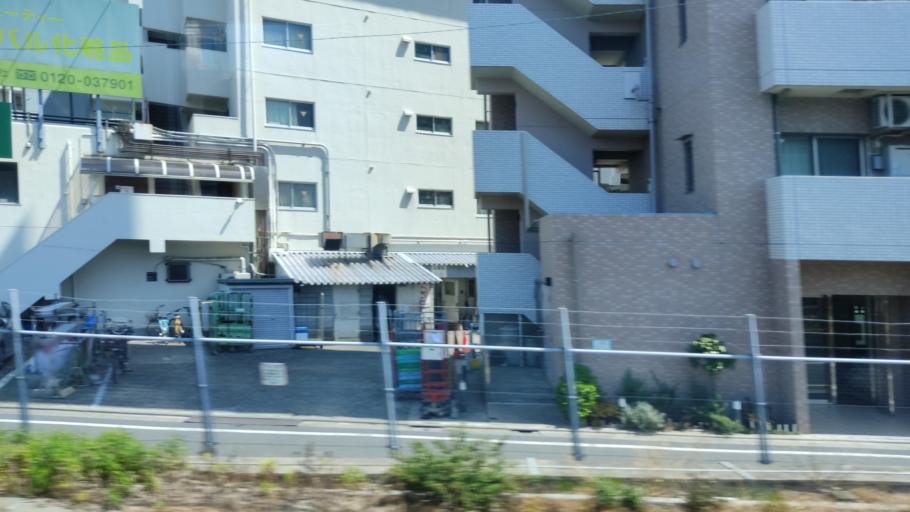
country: JP
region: Kanagawa
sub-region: Kawasaki-shi
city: Kawasaki
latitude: 35.5688
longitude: 139.7189
